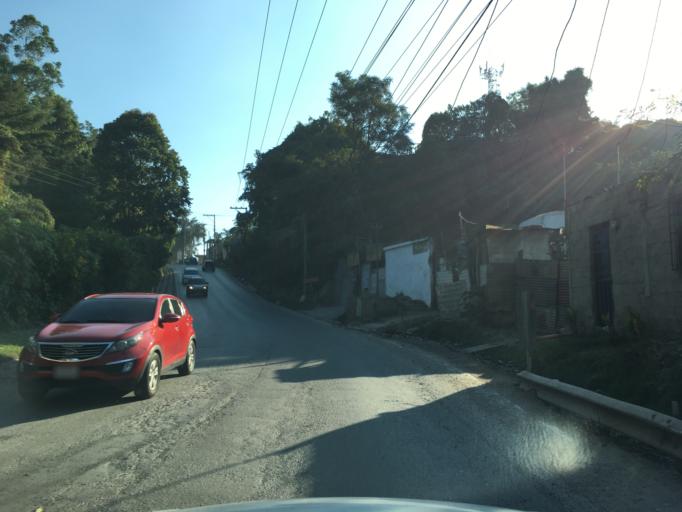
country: GT
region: Guatemala
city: Villa Nueva
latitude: 14.5348
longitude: -90.6165
